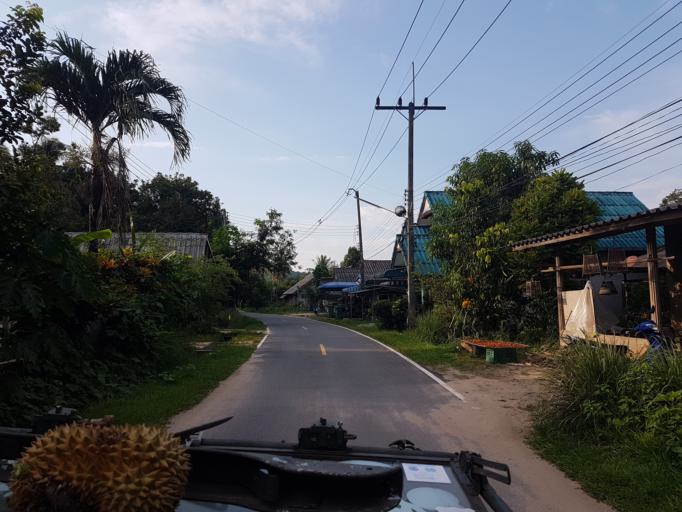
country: TH
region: Pattani
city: Khok Pho
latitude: 6.6734
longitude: 101.0950
